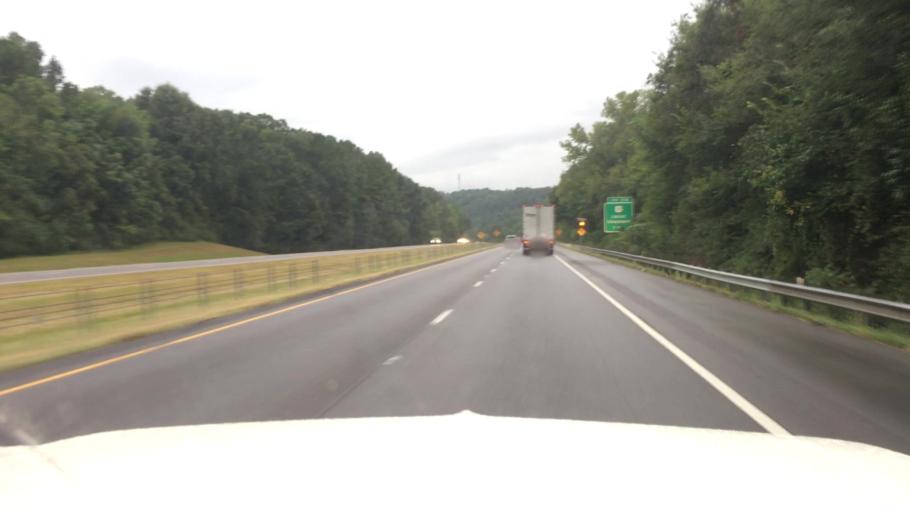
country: US
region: Alabama
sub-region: Morgan County
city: Falkville
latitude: 34.3342
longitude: -86.8972
